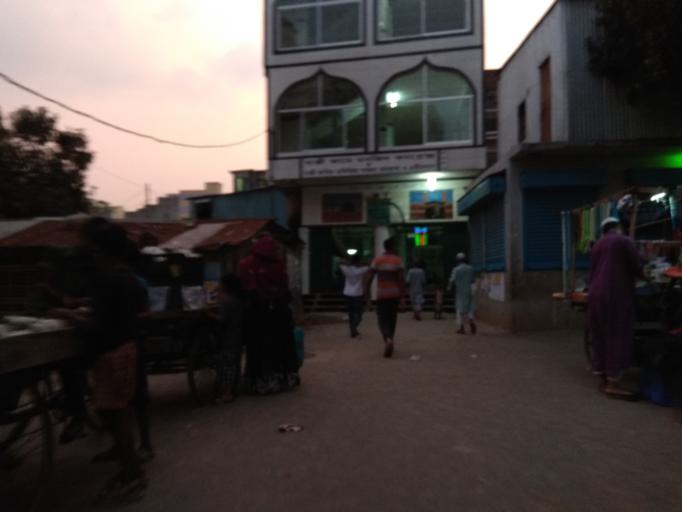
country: BD
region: Dhaka
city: Tungi
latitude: 23.8166
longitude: 90.3738
